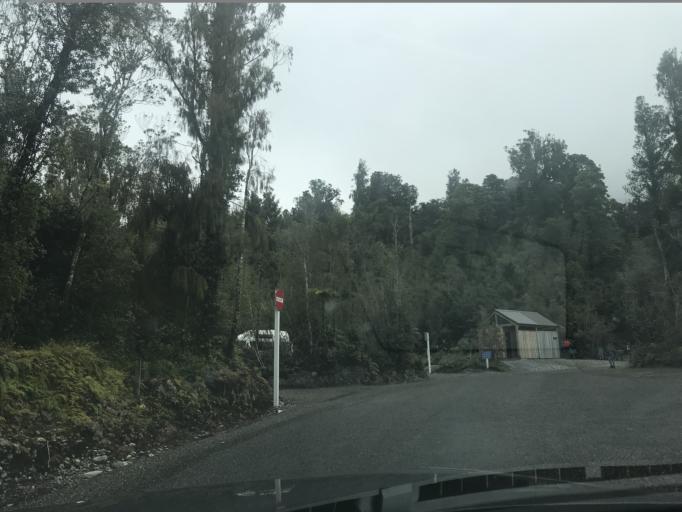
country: NZ
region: West Coast
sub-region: Westland District
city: Hokitika
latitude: -42.9565
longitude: 171.0201
